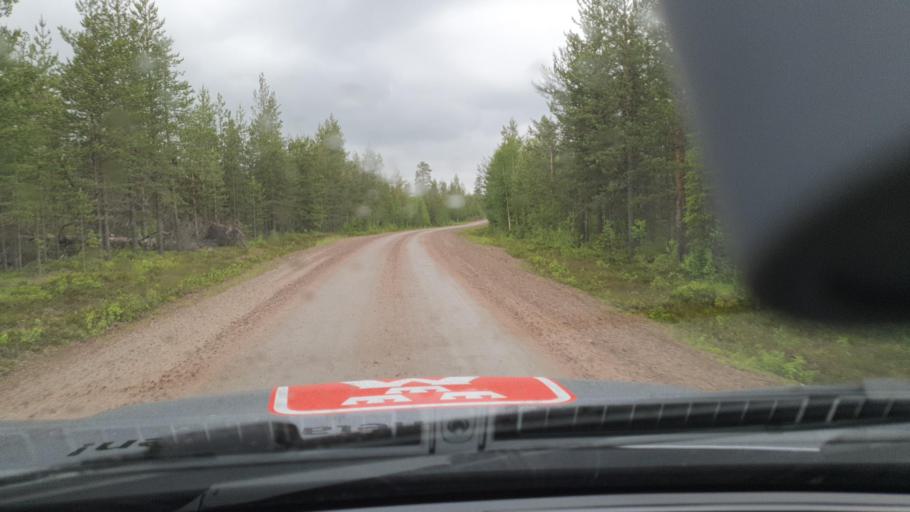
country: SE
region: Norrbotten
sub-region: Overkalix Kommun
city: OEverkalix
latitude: 66.6419
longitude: 22.7004
